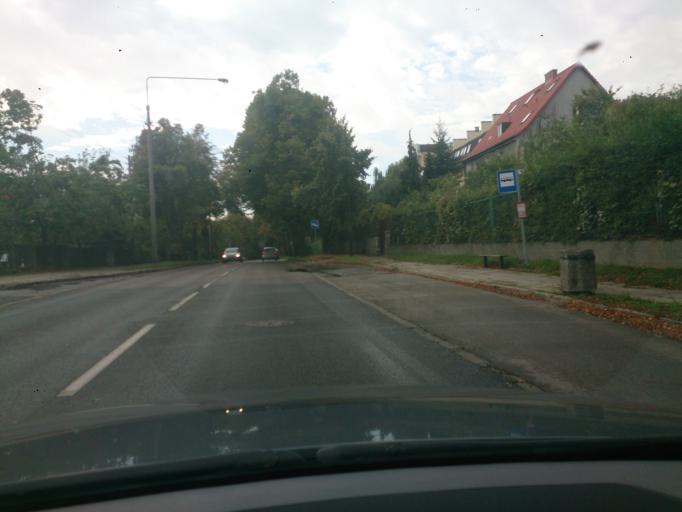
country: PL
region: Pomeranian Voivodeship
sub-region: Sopot
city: Sopot
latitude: 54.3981
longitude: 18.5640
